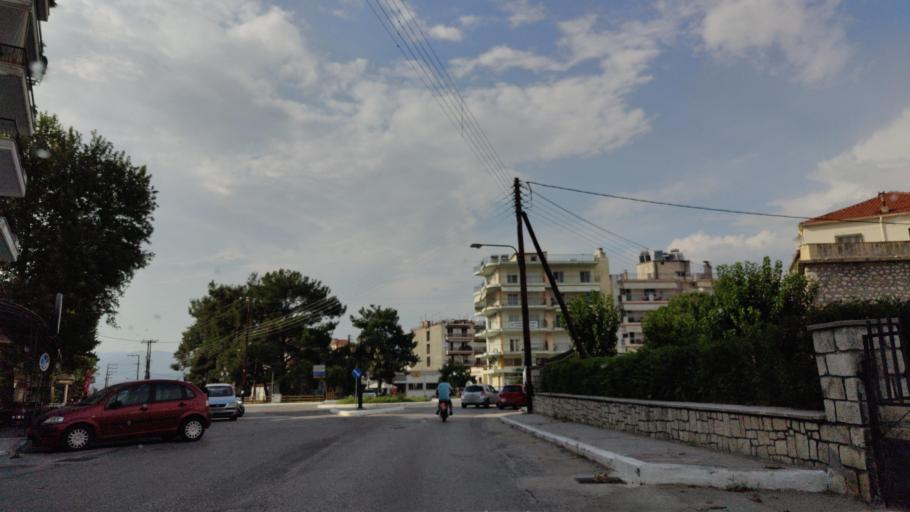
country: GR
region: Central Macedonia
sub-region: Nomos Serron
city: Sidirokastro
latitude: 41.2343
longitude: 23.3899
